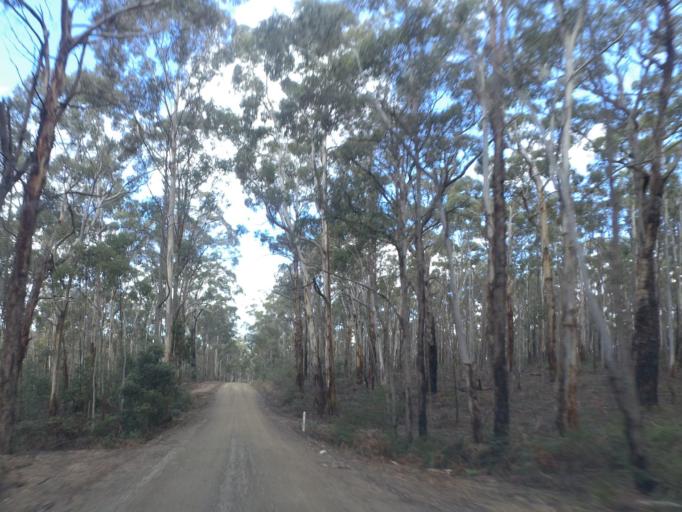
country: AU
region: Victoria
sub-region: Moorabool
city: Bacchus Marsh
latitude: -37.4648
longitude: 144.4803
